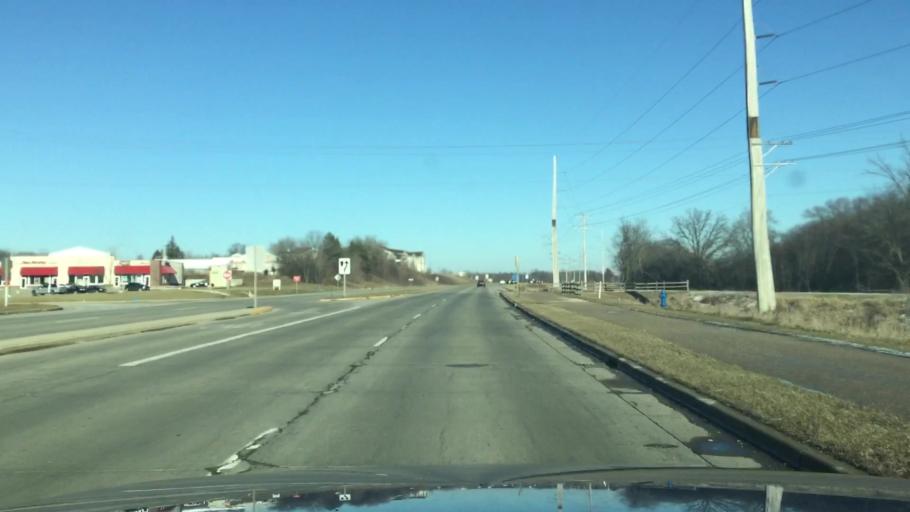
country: US
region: Wisconsin
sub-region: Racine County
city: Burlington
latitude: 42.6966
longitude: -88.2607
